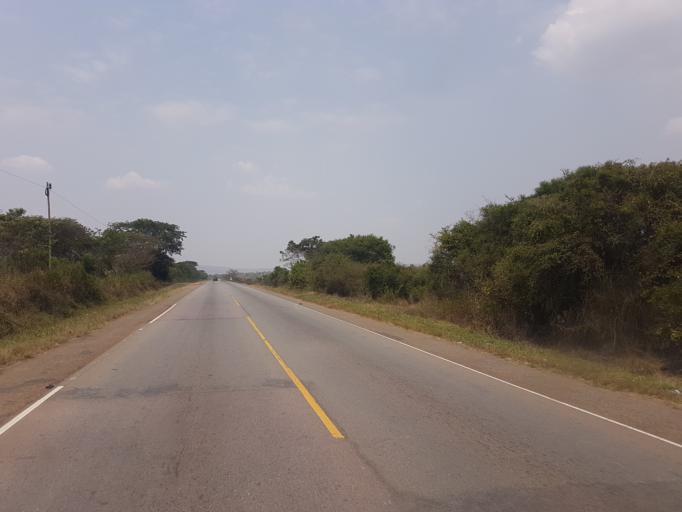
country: UG
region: Western Region
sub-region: Mbarara District
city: Mbarara
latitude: -0.5110
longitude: 30.7988
